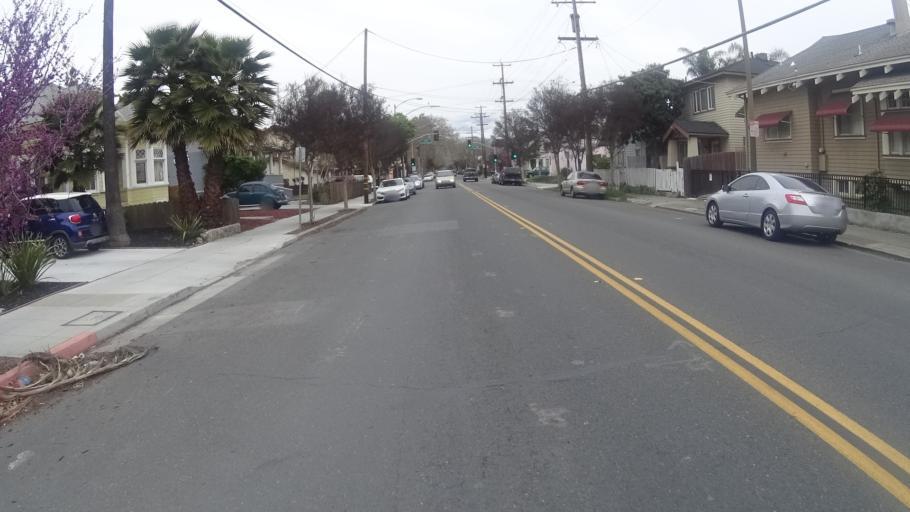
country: US
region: California
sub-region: Santa Clara County
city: San Jose
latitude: 37.3461
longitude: -121.8821
